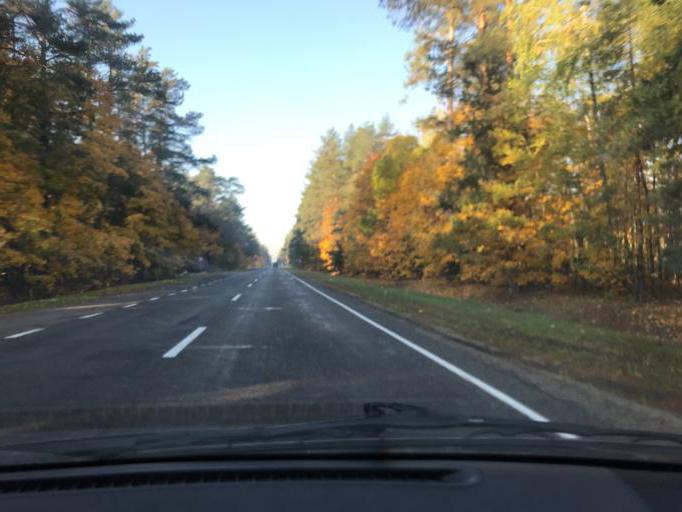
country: BY
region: Grodnenskaya
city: Zhyrovichy
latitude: 52.8660
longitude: 25.6929
